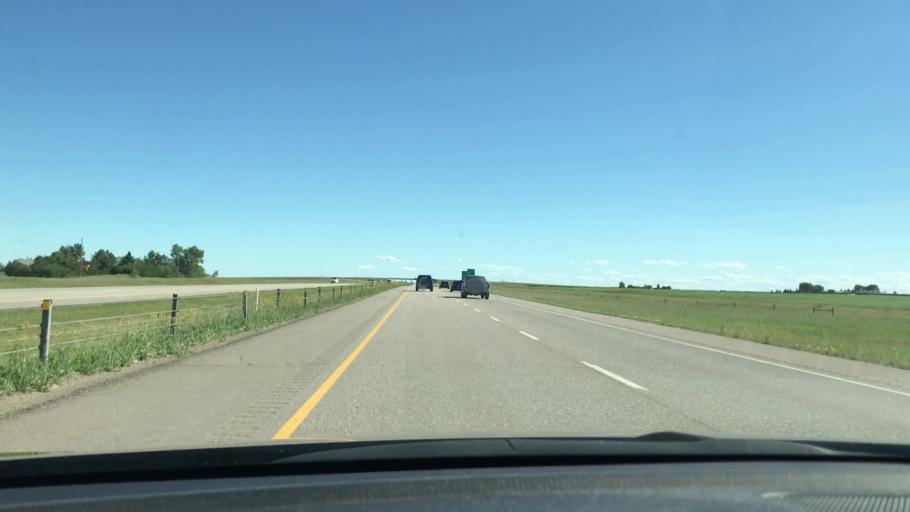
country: CA
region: Alberta
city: Didsbury
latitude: 51.6770
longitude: -114.0255
